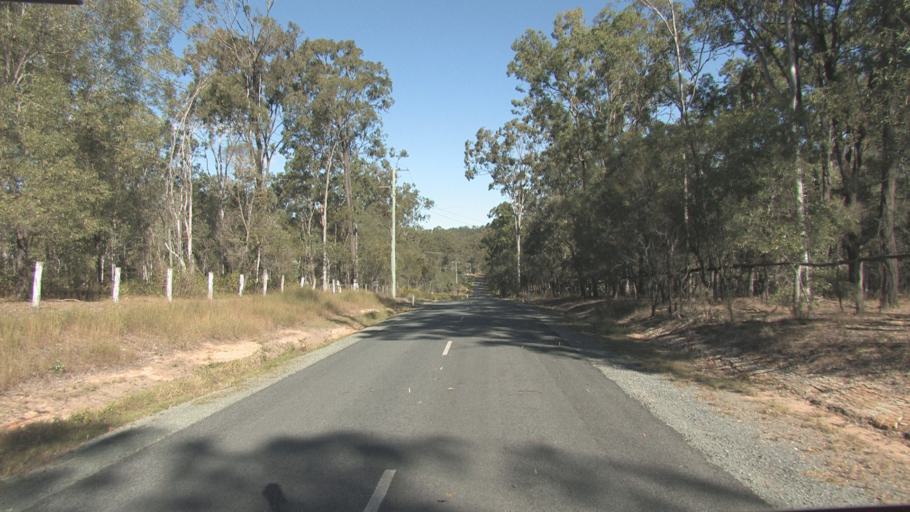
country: AU
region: Queensland
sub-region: Logan
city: Chambers Flat
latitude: -27.8118
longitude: 153.0717
